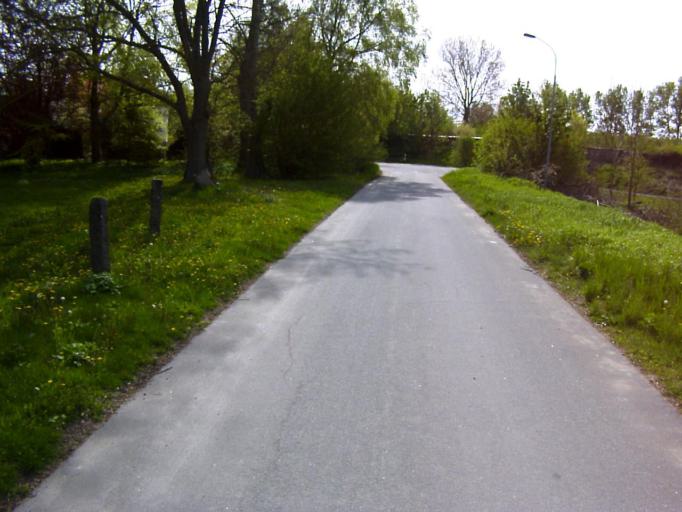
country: SE
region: Skane
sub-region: Kristianstads Kommun
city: Fjalkinge
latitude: 56.0359
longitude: 14.2775
